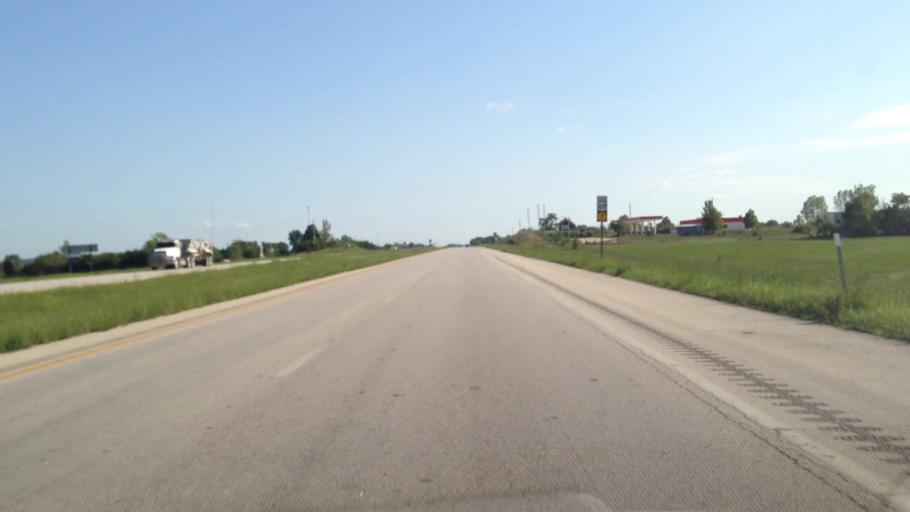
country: US
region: Kansas
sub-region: Bourbon County
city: Fort Scott
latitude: 37.8004
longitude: -94.7052
